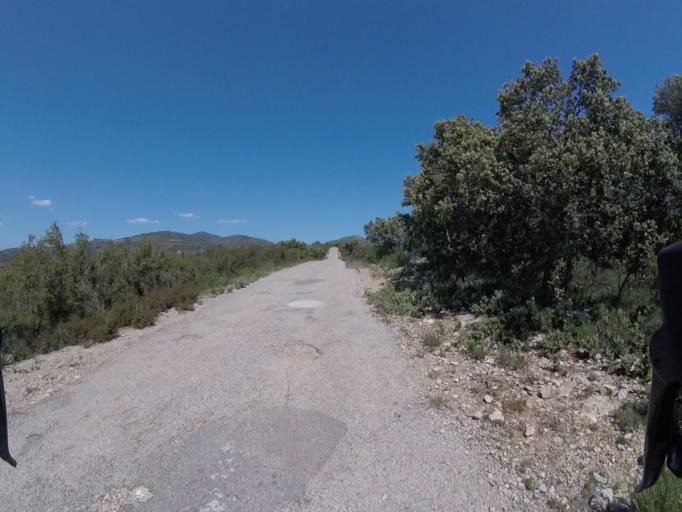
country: ES
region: Valencia
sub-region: Provincia de Castello
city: Sierra-Engarceran
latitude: 40.2309
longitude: -0.0246
